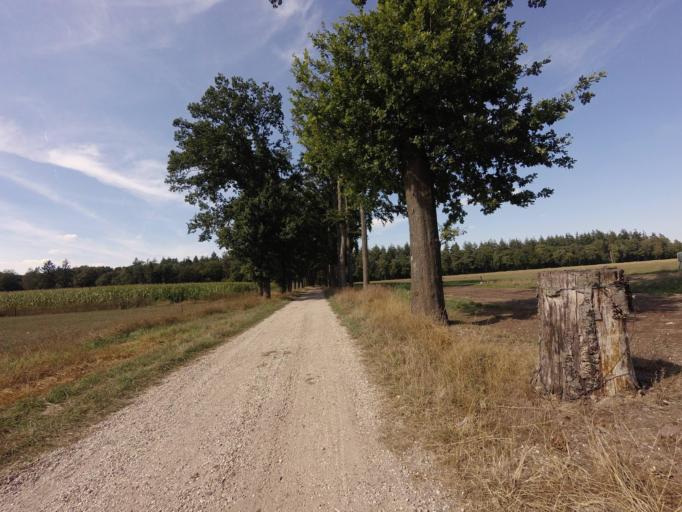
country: NL
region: Gelderland
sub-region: Gemeente Apeldoorn
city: Loenen
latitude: 52.1377
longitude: 6.0303
